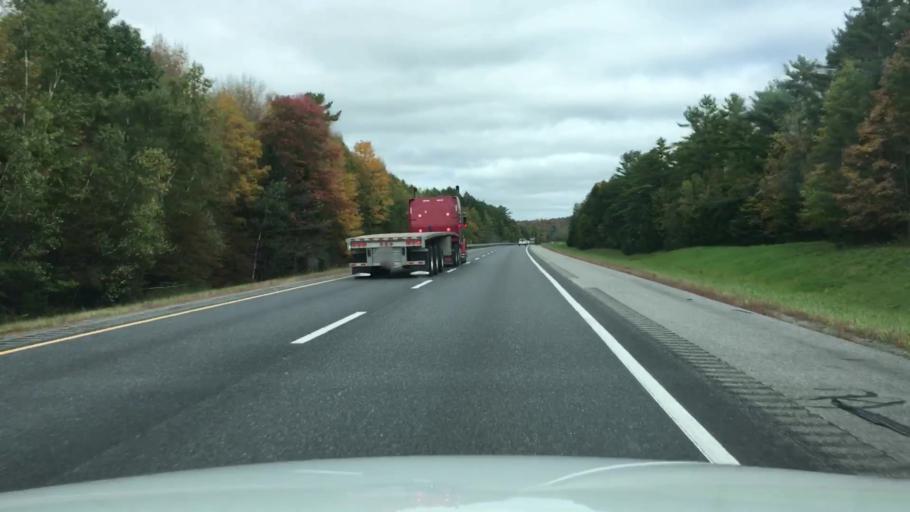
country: US
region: Maine
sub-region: Sagadahoc County
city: Richmond
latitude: 44.0549
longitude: -69.8874
